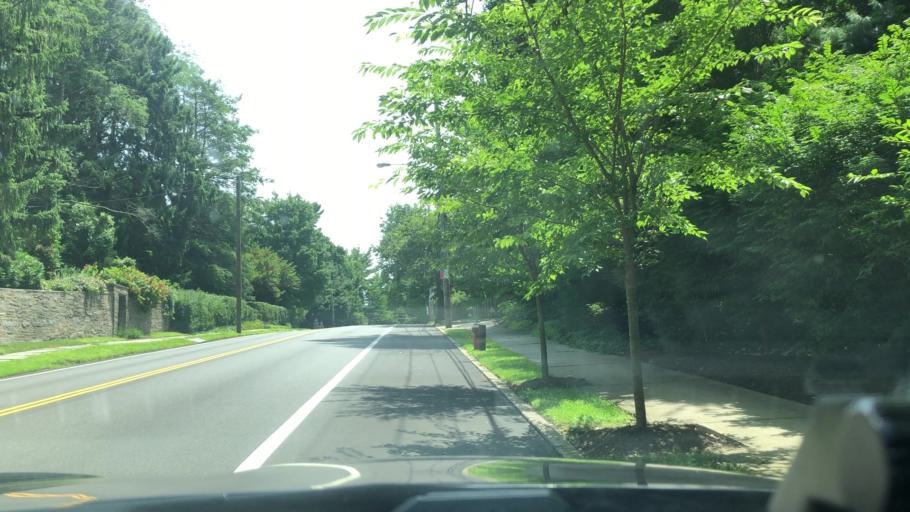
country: US
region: Pennsylvania
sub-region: Montgomery County
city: Wyndmoor
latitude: 40.0828
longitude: -75.2093
